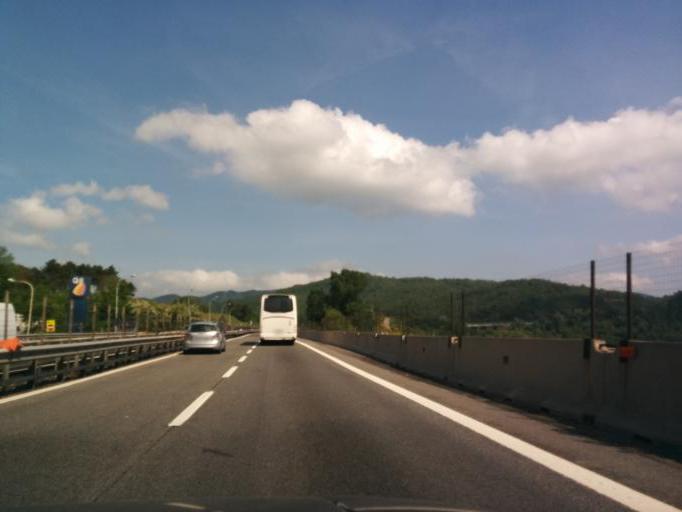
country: IT
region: Tuscany
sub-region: Province of Florence
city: Barberino di Mugello
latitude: 44.0327
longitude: 11.2250
